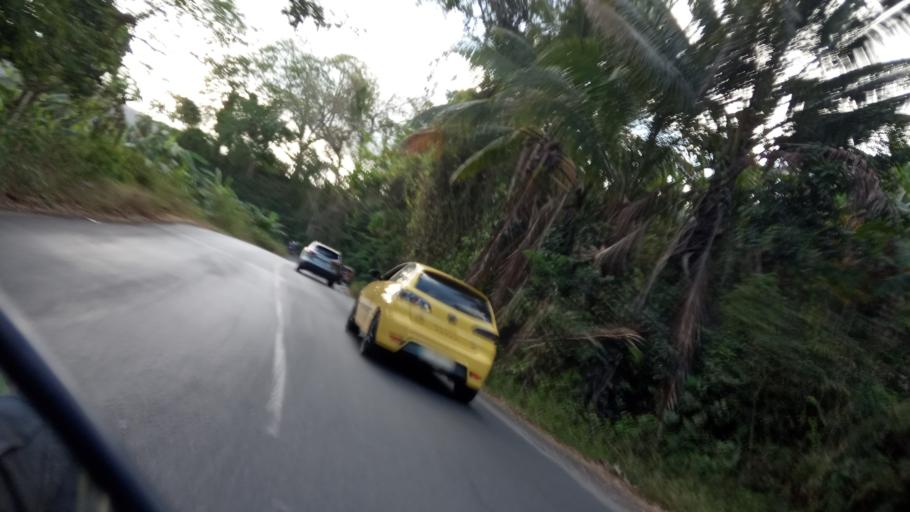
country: YT
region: Dembeni
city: Dembeni
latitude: -12.8369
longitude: 45.1816
